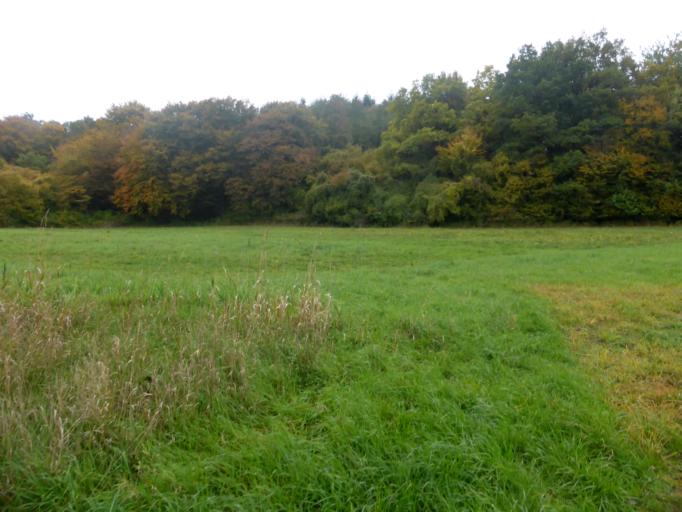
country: LU
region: Grevenmacher
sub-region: Canton de Grevenmacher
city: Mertert
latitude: 49.7159
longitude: 6.4648
